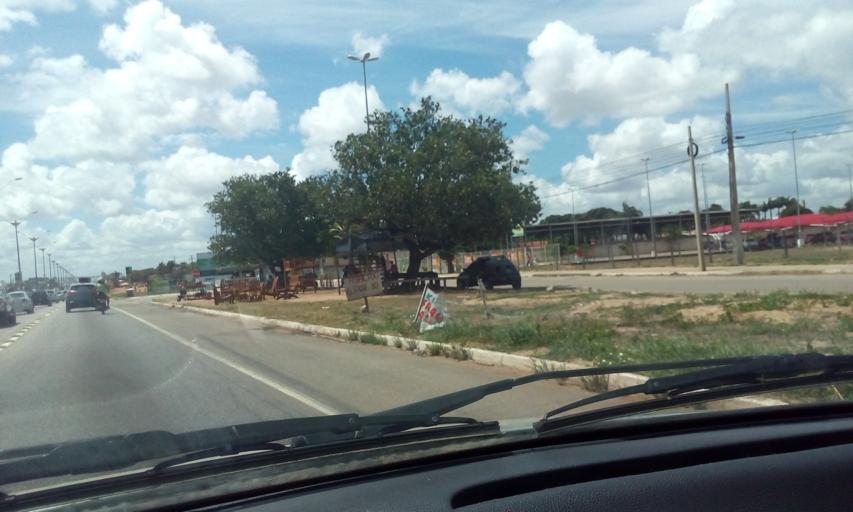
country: BR
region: Rio Grande do Norte
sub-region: Parnamirim
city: Parnamirim
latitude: -5.9013
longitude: -35.2594
